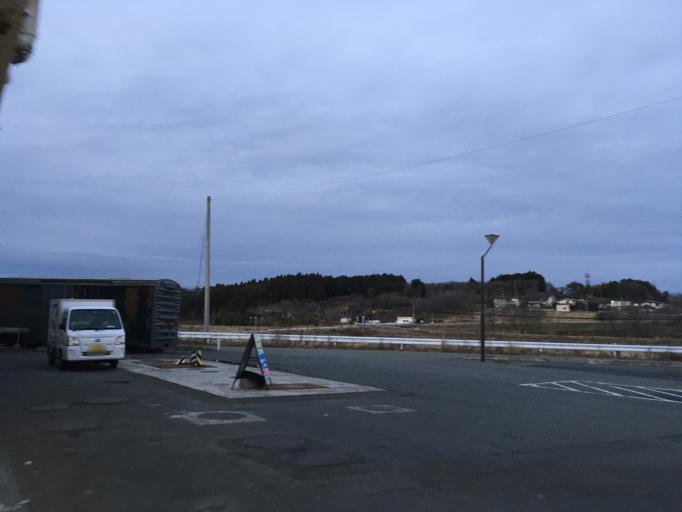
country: JP
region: Miyagi
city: Kogota
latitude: 38.6508
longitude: 141.0767
